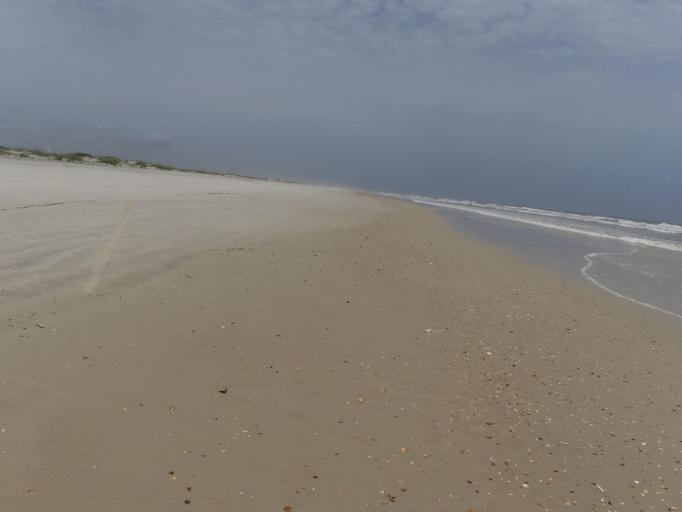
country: US
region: Florida
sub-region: Saint Johns County
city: Saint Augustine
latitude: 29.8986
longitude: -81.2765
